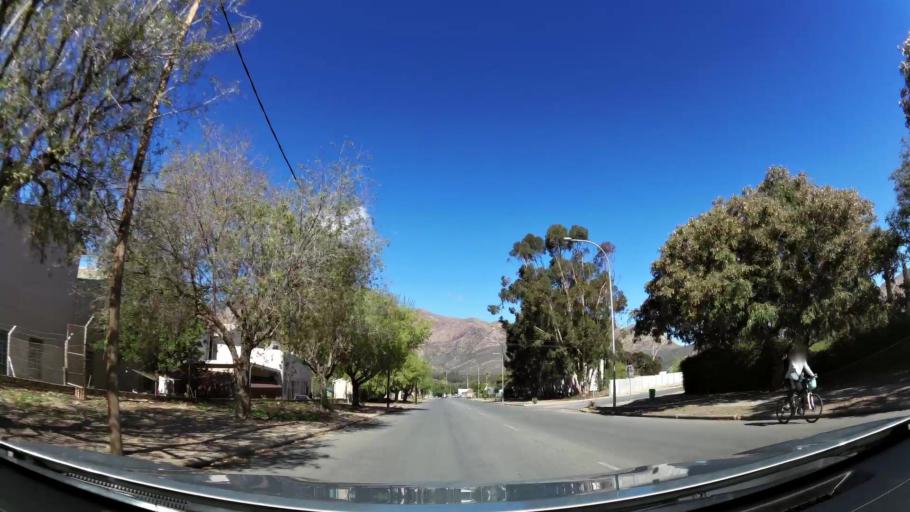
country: ZA
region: Western Cape
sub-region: Cape Winelands District Municipality
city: Ashton
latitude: -33.7820
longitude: 20.1304
